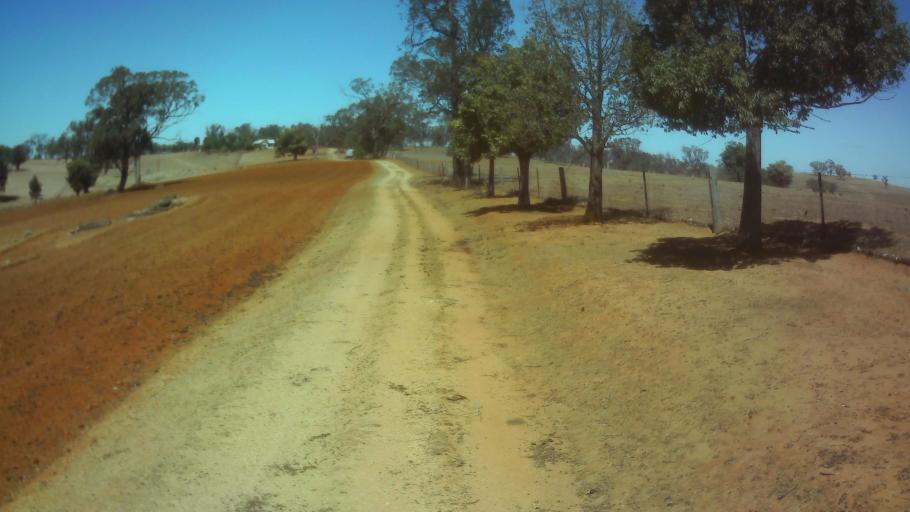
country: AU
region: New South Wales
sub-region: Cowra
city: Cowra
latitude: -33.9064
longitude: 148.5081
